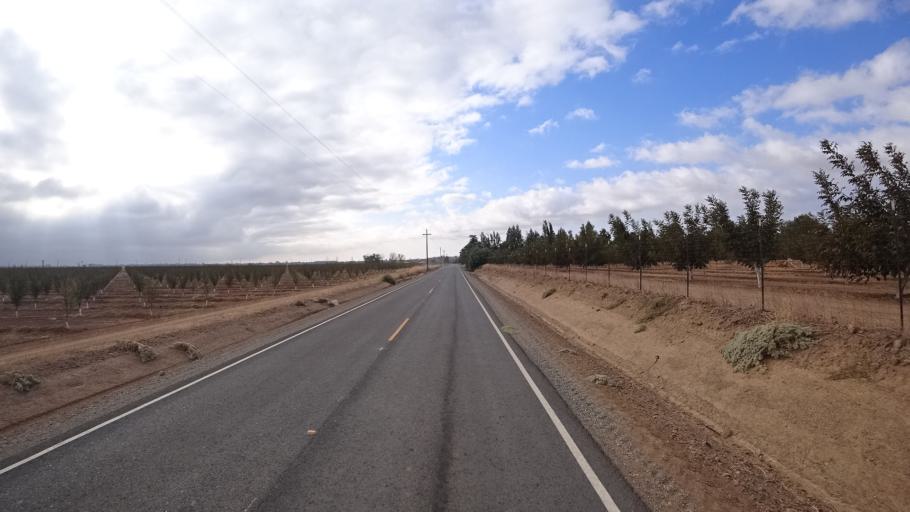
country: US
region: California
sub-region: Yolo County
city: Esparto
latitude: 38.7226
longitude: -122.0466
